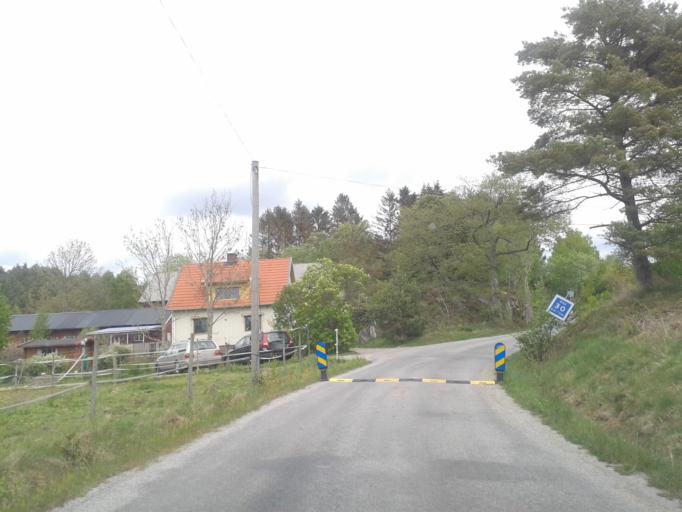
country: SE
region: Vaestra Goetaland
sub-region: Kungalvs Kommun
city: Kode
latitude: 57.8891
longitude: 11.8860
